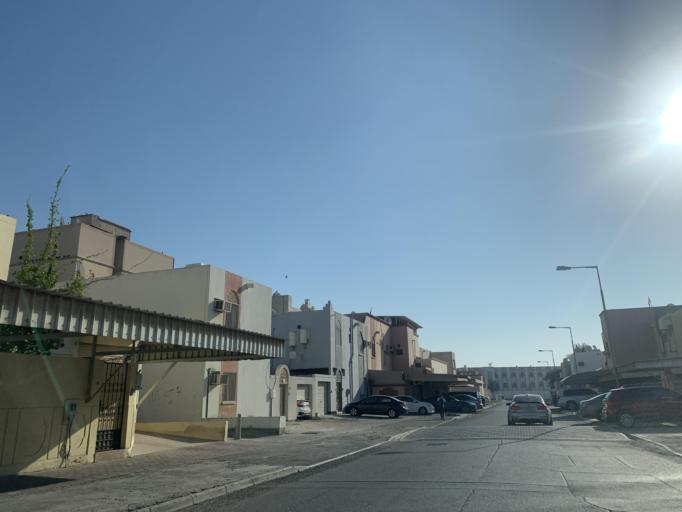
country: BH
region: Central Governorate
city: Madinat Hamad
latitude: 26.1101
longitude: 50.5086
